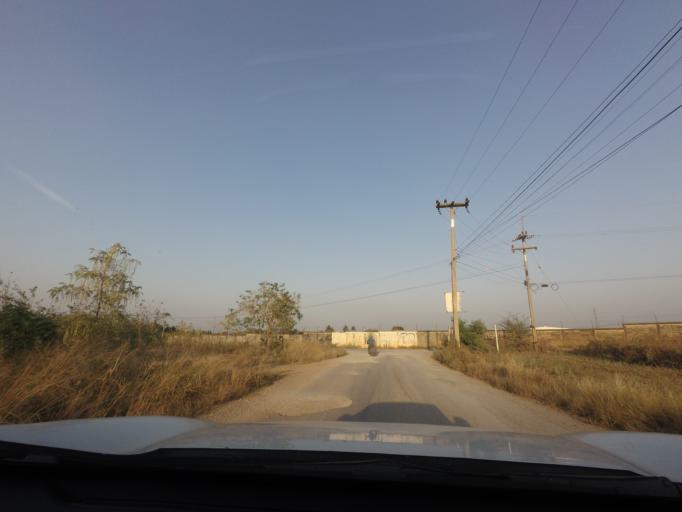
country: TH
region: Nakhon Ratchasima
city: Pak Chong
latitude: 14.6453
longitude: 101.3769
